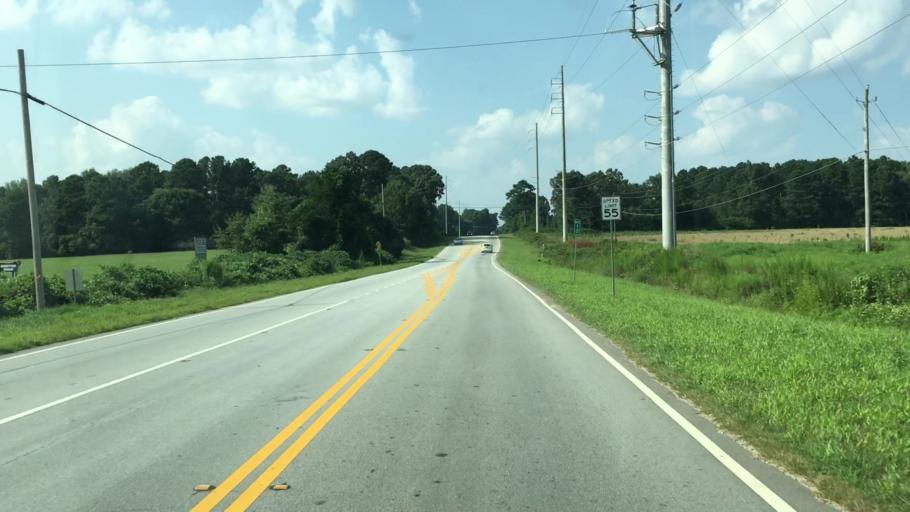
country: US
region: Georgia
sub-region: Walton County
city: Social Circle
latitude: 33.6024
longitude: -83.7510
